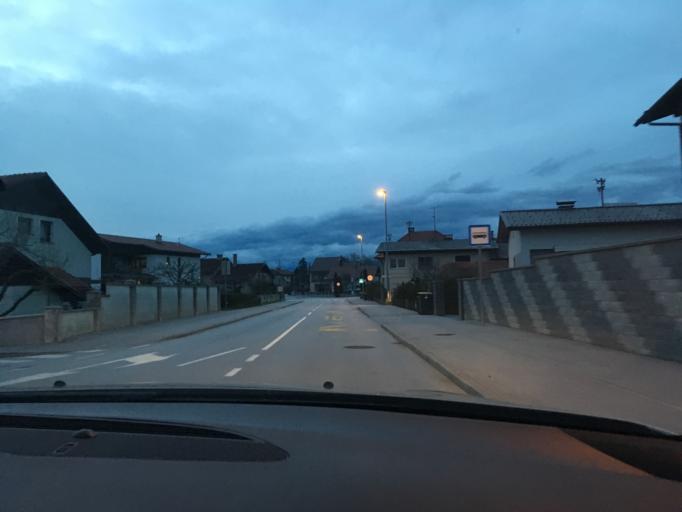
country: SI
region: Domzale
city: Vir
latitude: 46.1479
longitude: 14.6072
